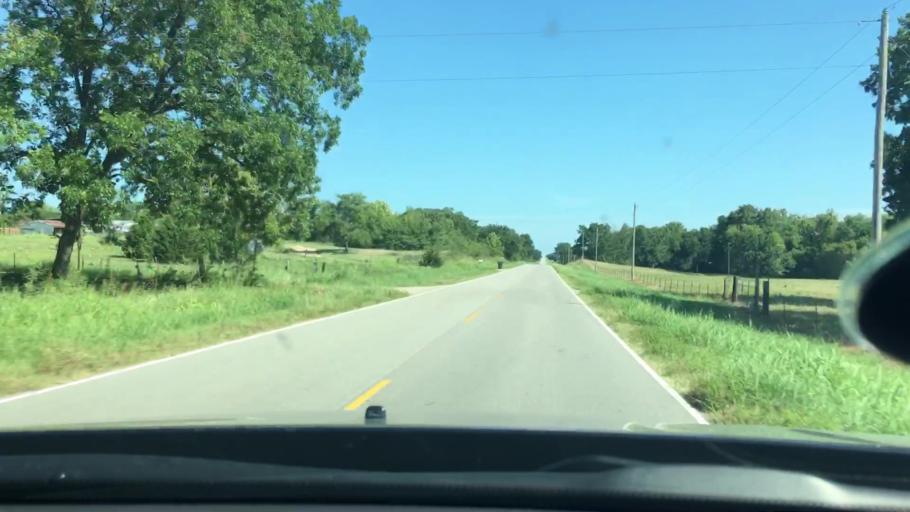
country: US
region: Oklahoma
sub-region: Johnston County
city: Tishomingo
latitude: 34.2845
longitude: -96.5487
